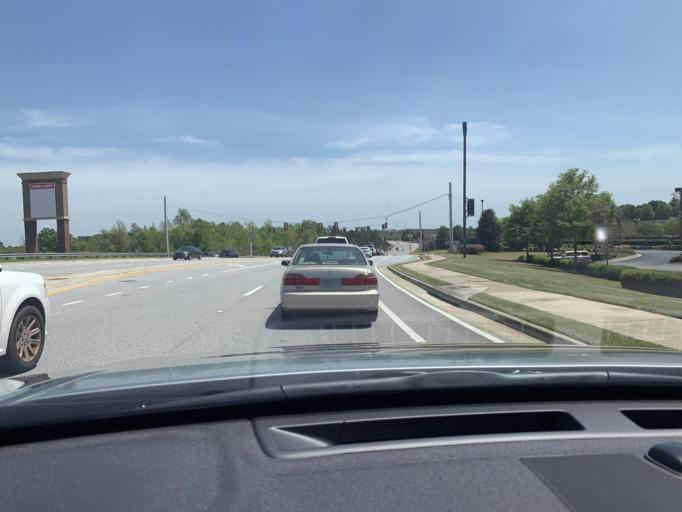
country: US
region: Georgia
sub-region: Oconee County
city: Watkinsville
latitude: 33.9182
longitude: -83.4558
